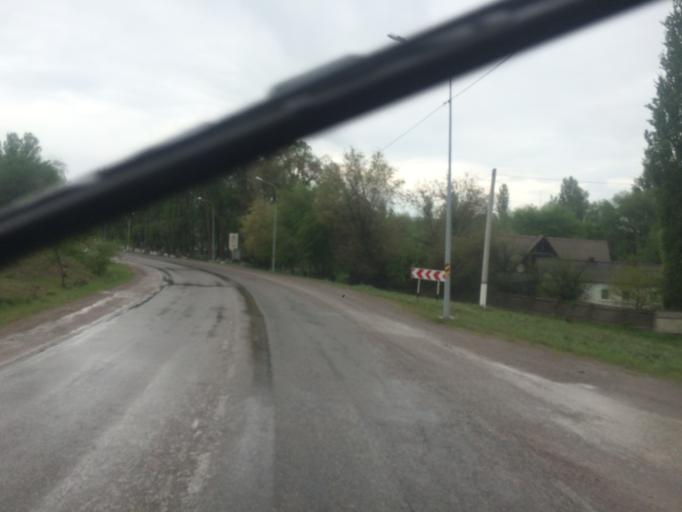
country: KZ
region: Zhambyl
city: Georgiyevka
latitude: 43.2330
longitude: 74.7605
